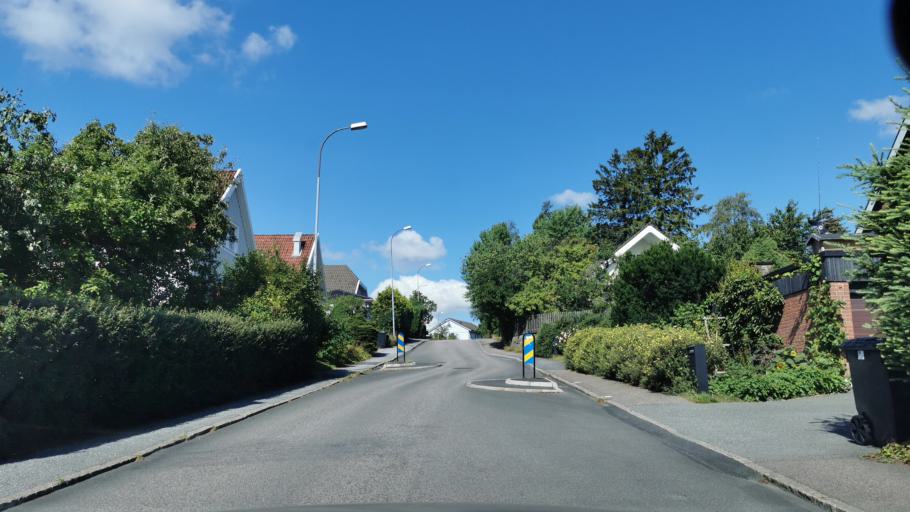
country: SE
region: Vaestra Goetaland
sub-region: Molndal
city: Moelndal
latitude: 57.6746
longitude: 11.9891
